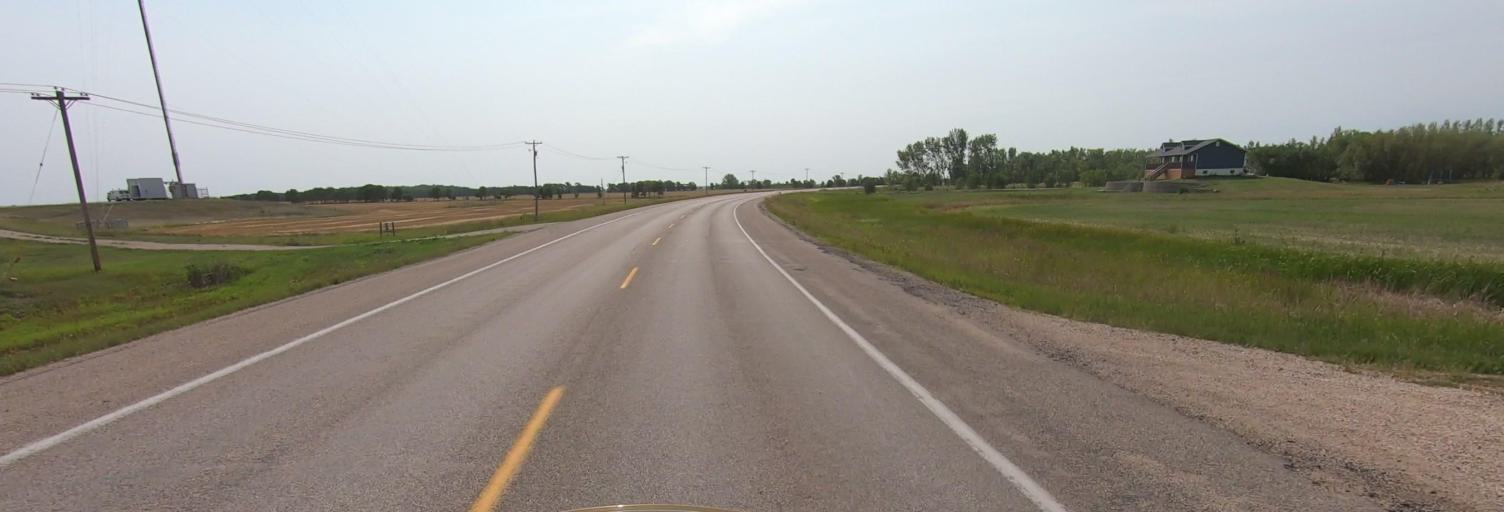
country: CA
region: Manitoba
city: Niverville
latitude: 49.6611
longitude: -97.1035
